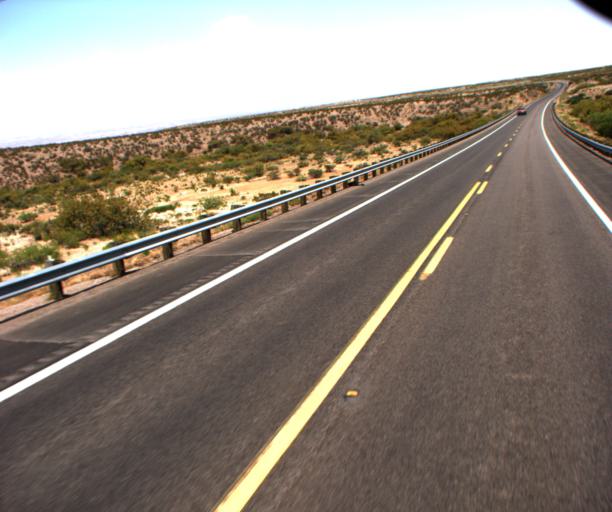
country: US
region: Arizona
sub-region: Greenlee County
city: Clifton
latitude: 32.7267
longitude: -109.1768
